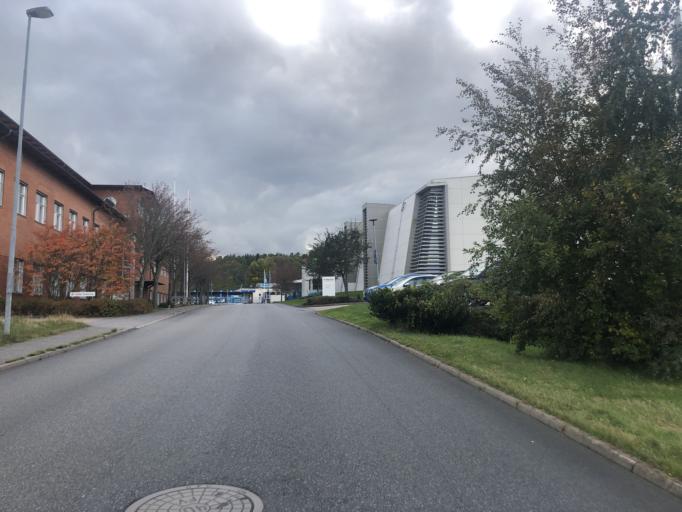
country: SE
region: Vaestra Goetaland
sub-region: Molndal
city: Moelndal
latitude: 57.6420
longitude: 11.9878
